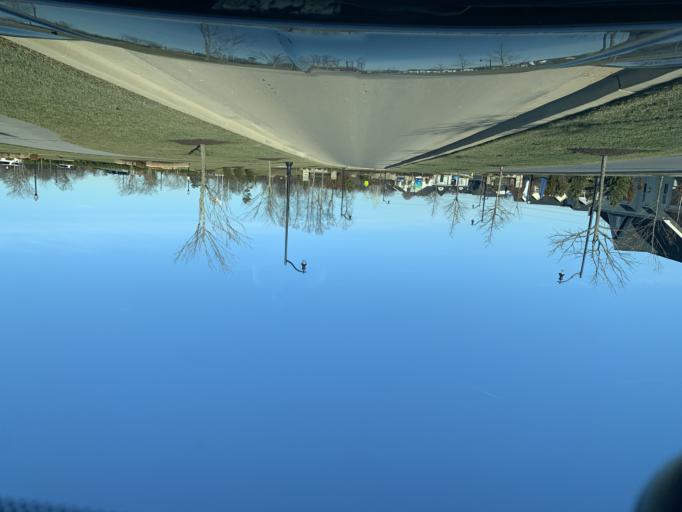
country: US
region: Maryland
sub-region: Anne Arundel County
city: Crofton
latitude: 39.0261
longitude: -76.7270
